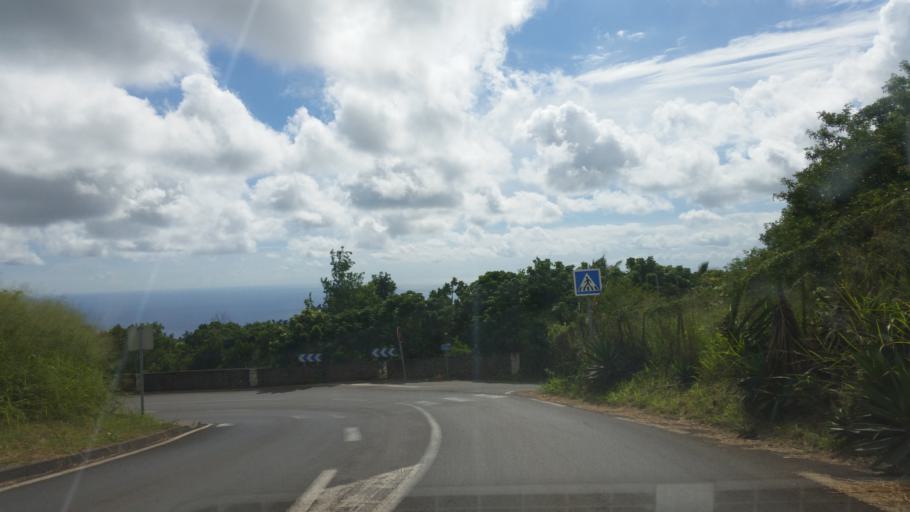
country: RE
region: Reunion
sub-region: Reunion
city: Trois-Bassins
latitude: -21.0679
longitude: 55.2660
